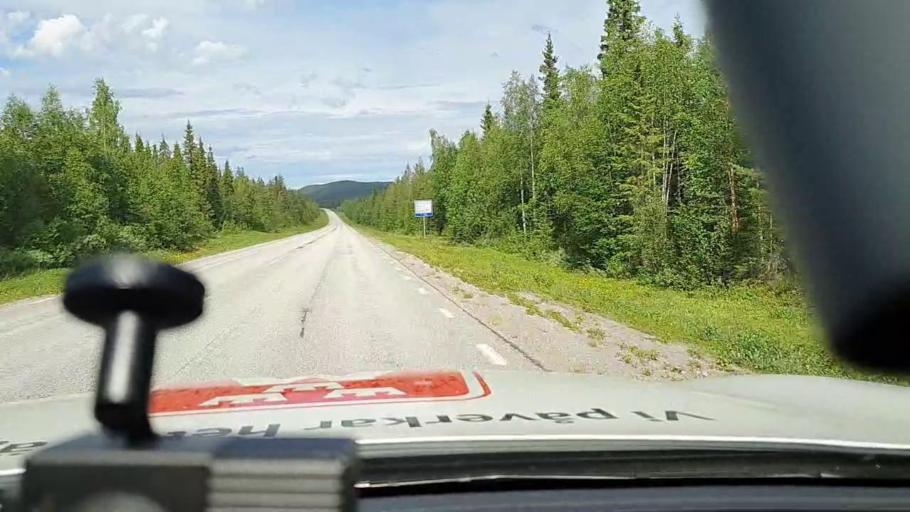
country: SE
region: Norrbotten
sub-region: Jokkmokks Kommun
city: Jokkmokk
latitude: 66.5463
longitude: 20.1325
